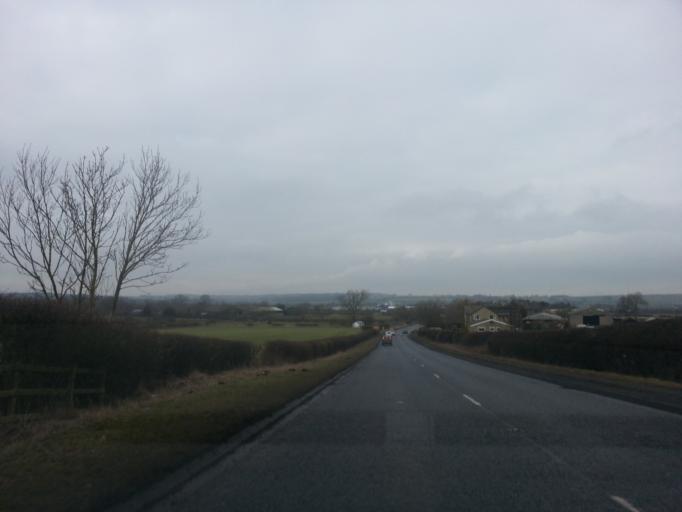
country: GB
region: England
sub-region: County Durham
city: Bishop Auckland
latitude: 54.6208
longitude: -1.7068
